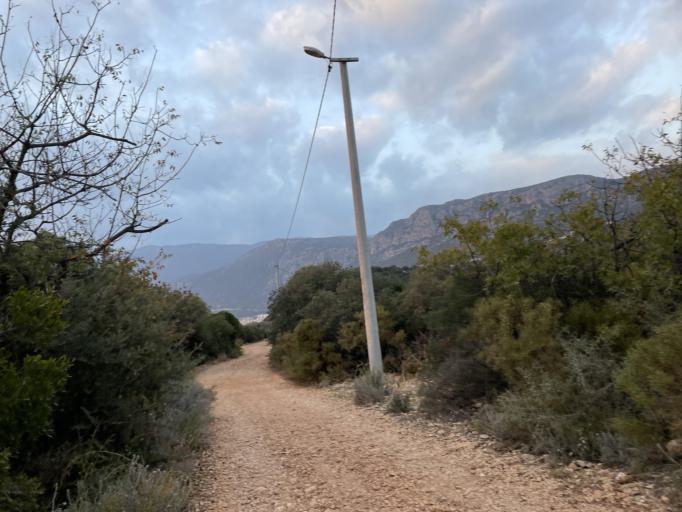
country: TR
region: Antalya
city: Kas
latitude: 36.1842
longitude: 29.6525
